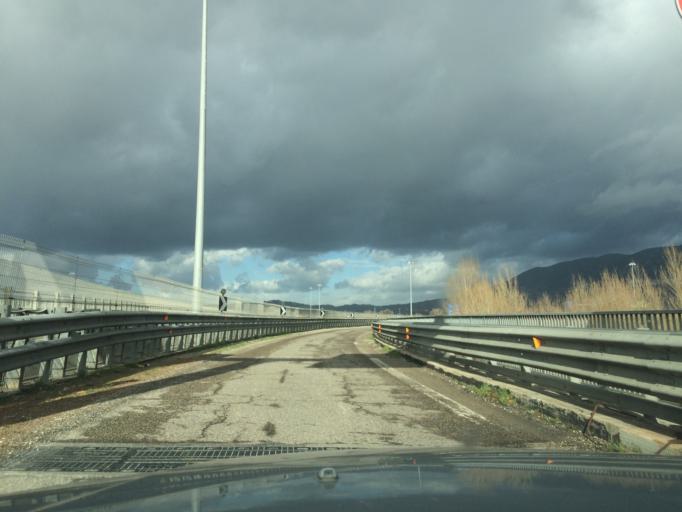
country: IT
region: Umbria
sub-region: Provincia di Terni
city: San Gemini
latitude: 42.5665
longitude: 12.5781
